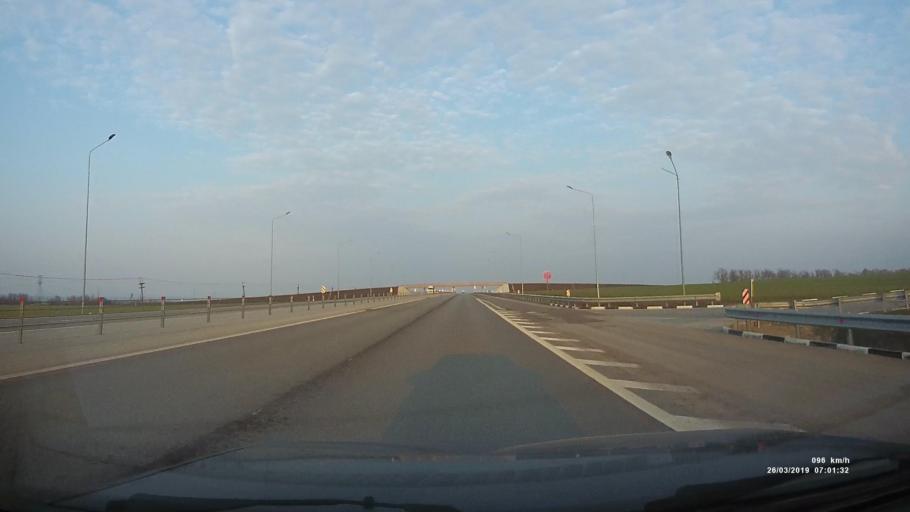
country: RU
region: Rostov
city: Sinyavskoye
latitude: 47.2958
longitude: 39.2571
